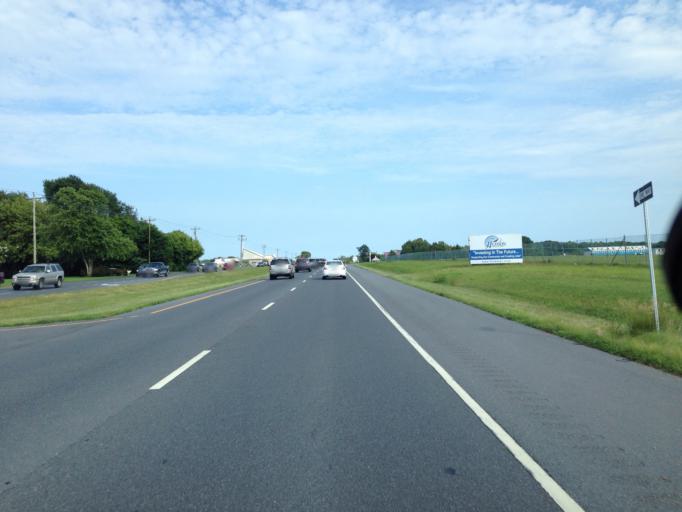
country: US
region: Delaware
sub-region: Sussex County
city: Milton
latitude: 38.7787
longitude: -75.2319
